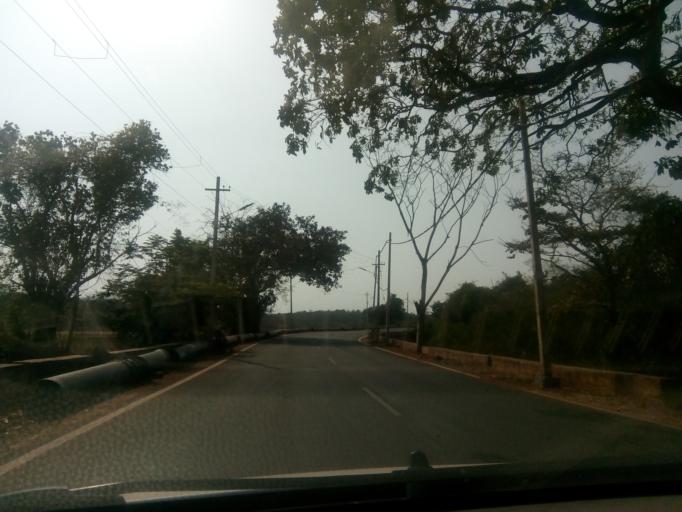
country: IN
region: Goa
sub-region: North Goa
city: Pernem
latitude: 15.7183
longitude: 73.8552
